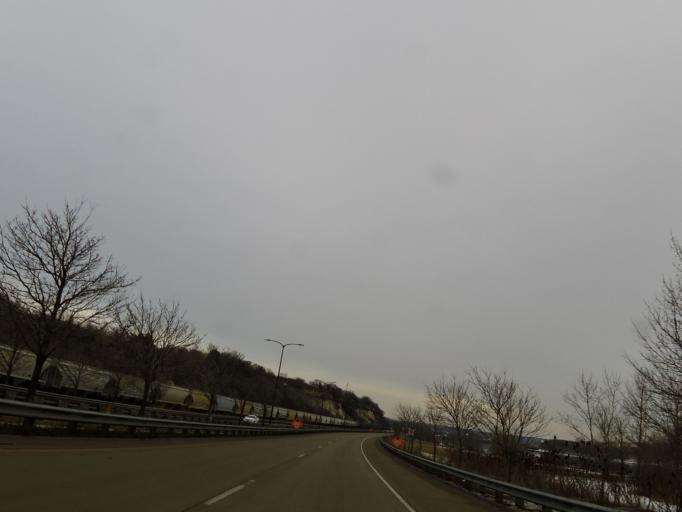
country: US
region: Minnesota
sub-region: Ramsey County
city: Saint Paul
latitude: 44.9492
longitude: -93.0726
